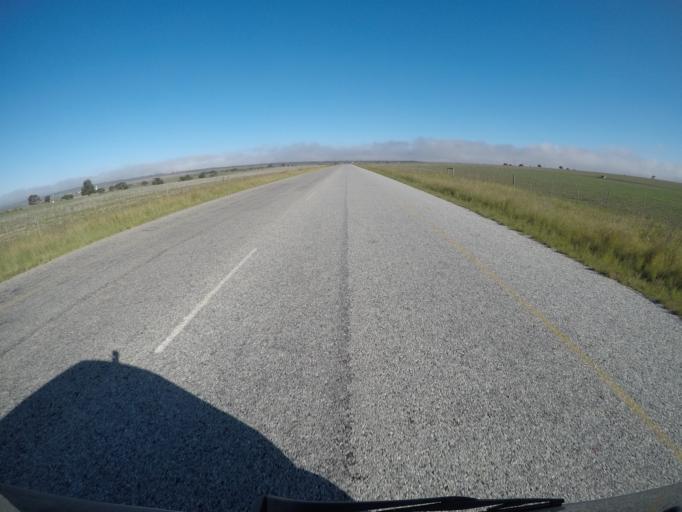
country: ZA
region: Western Cape
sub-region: Eden District Municipality
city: Mossel Bay
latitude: -34.1752
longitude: 22.0153
